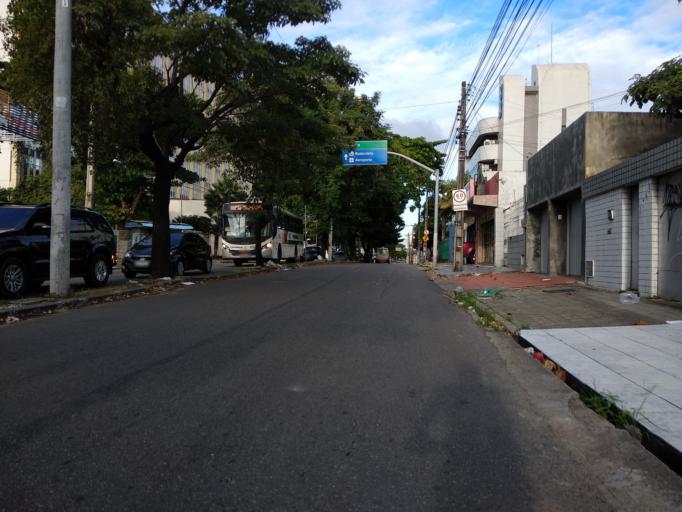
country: BR
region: Ceara
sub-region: Fortaleza
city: Fortaleza
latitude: -3.7285
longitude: -38.5400
